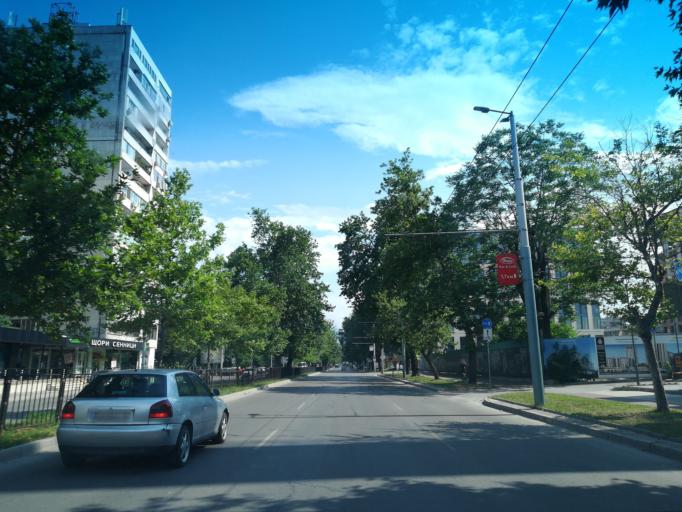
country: BG
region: Plovdiv
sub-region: Obshtina Plovdiv
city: Plovdiv
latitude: 42.1438
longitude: 24.7631
